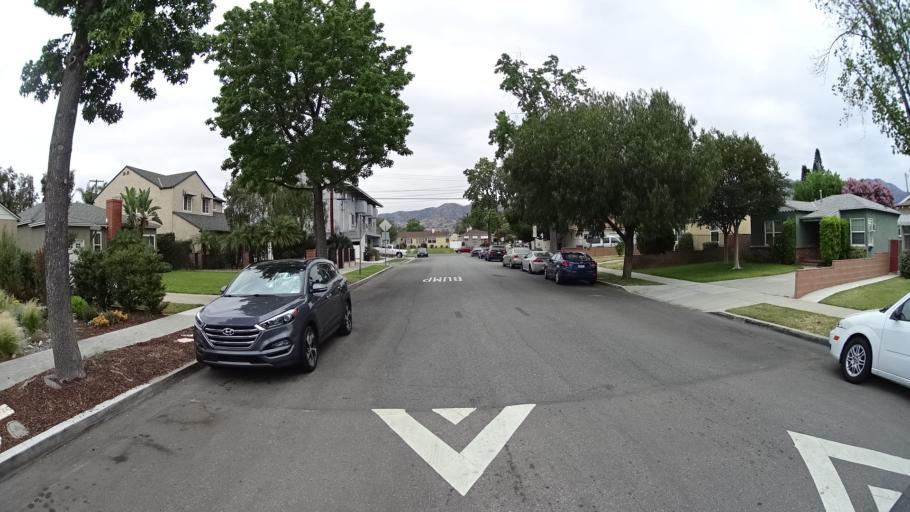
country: US
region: California
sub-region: Los Angeles County
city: Burbank
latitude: 34.1836
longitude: -118.3265
